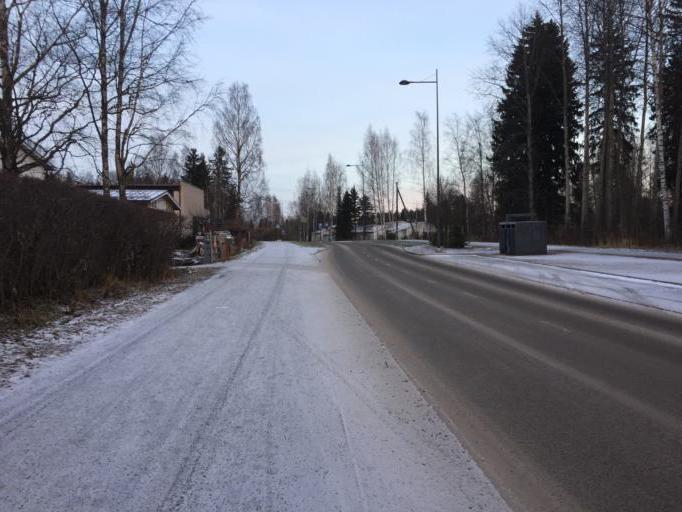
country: FI
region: Uusimaa
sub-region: Helsinki
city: Kauniainen
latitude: 60.2390
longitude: 24.7447
